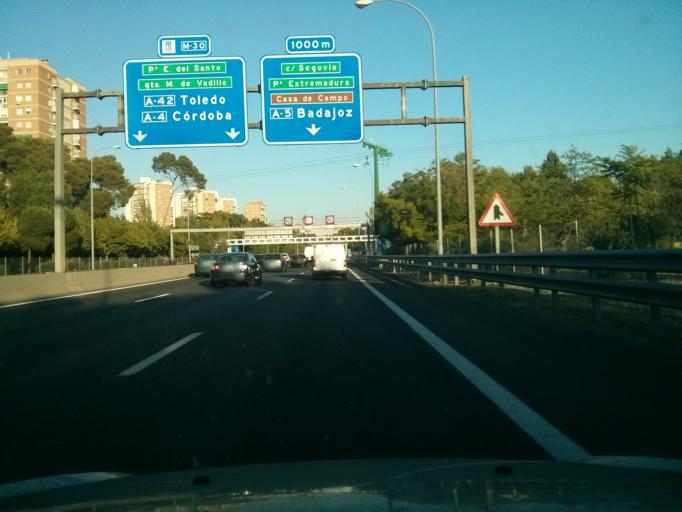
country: ES
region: Madrid
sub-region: Provincia de Madrid
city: Moncloa-Aravaca
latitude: 40.4262
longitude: -3.7335
